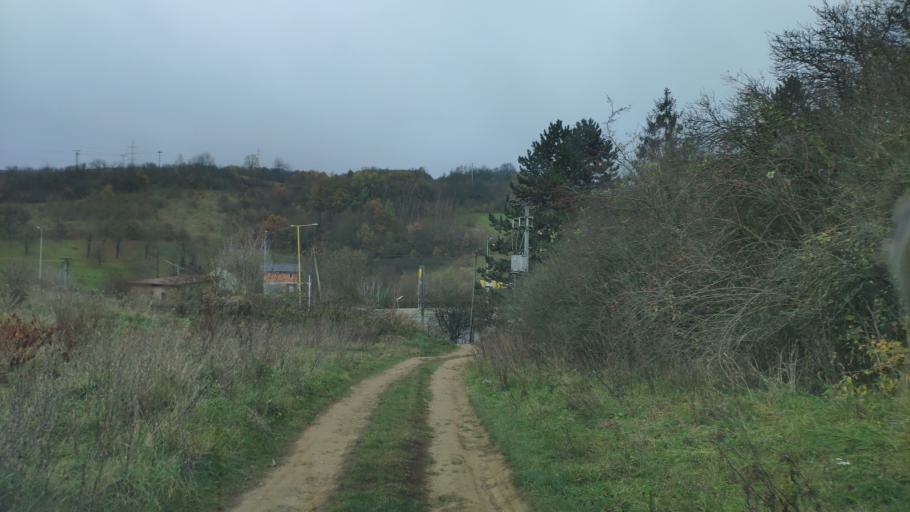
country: SK
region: Presovsky
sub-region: Okres Presov
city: Presov
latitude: 49.0008
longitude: 21.2068
